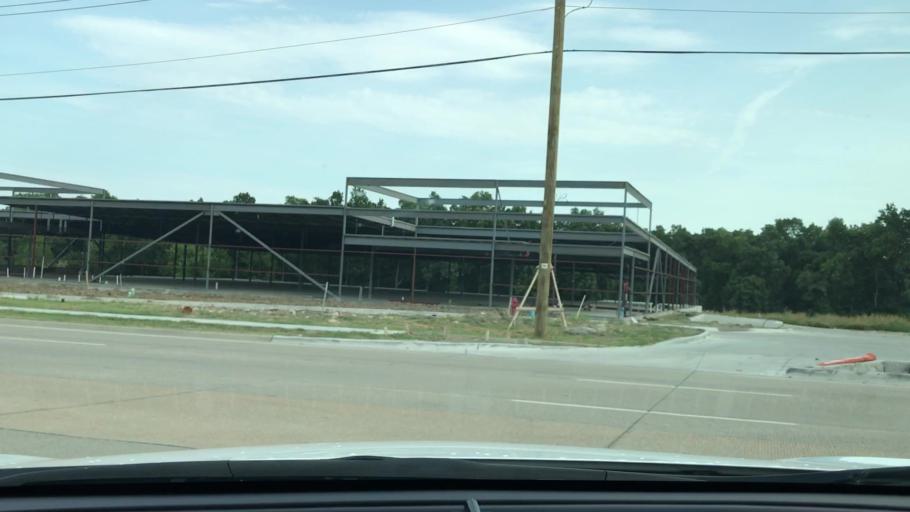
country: US
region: Texas
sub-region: Dallas County
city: Rowlett
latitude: 32.9079
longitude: -96.5537
